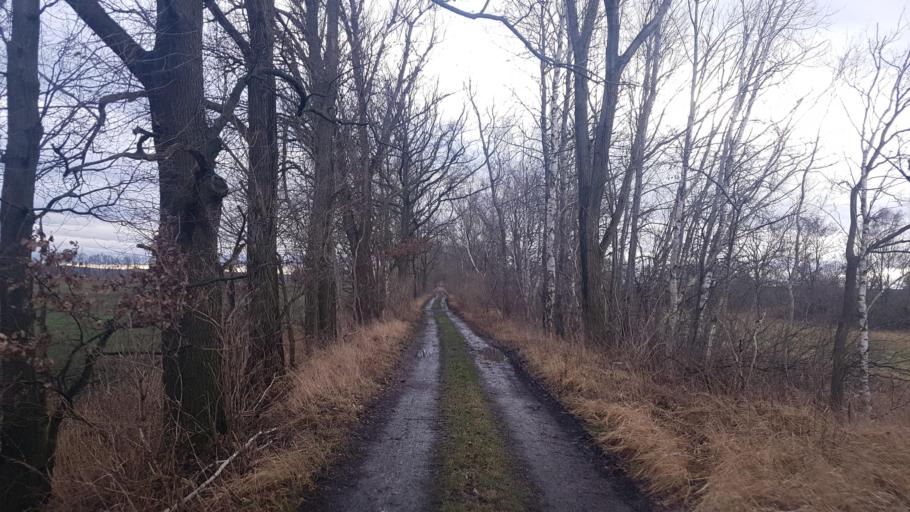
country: DE
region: Brandenburg
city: Plessa
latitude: 51.4324
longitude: 13.6497
